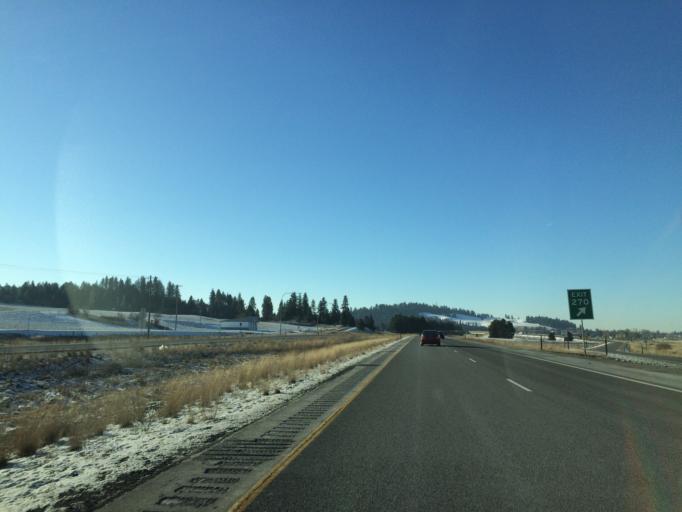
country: US
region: Washington
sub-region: Spokane County
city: Airway Heights
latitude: 47.5704
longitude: -117.5880
